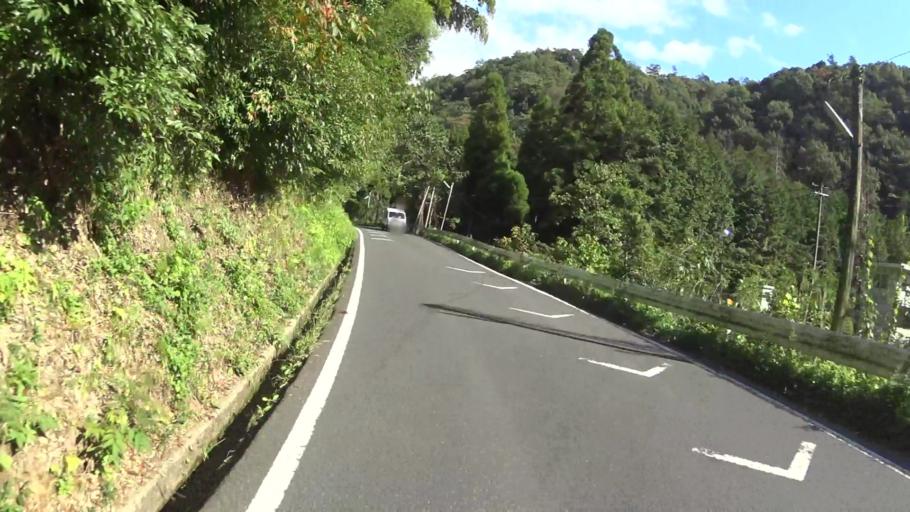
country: JP
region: Kyoto
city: Miyazu
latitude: 35.5780
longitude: 135.1611
